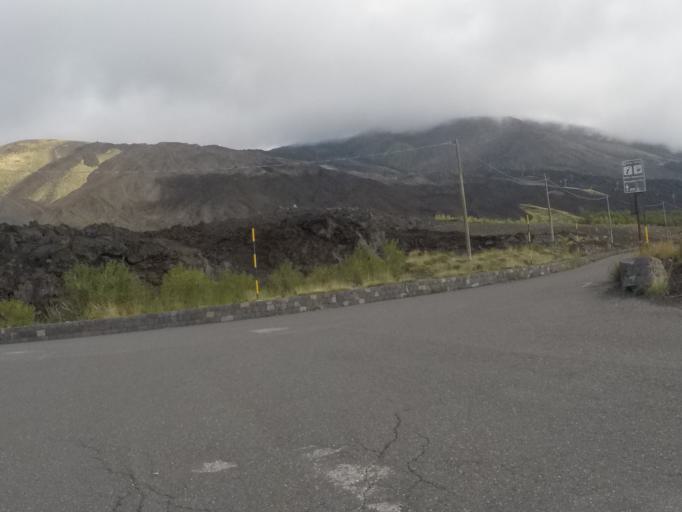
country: IT
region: Sicily
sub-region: Catania
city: Ragalna
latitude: 37.6991
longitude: 14.9944
